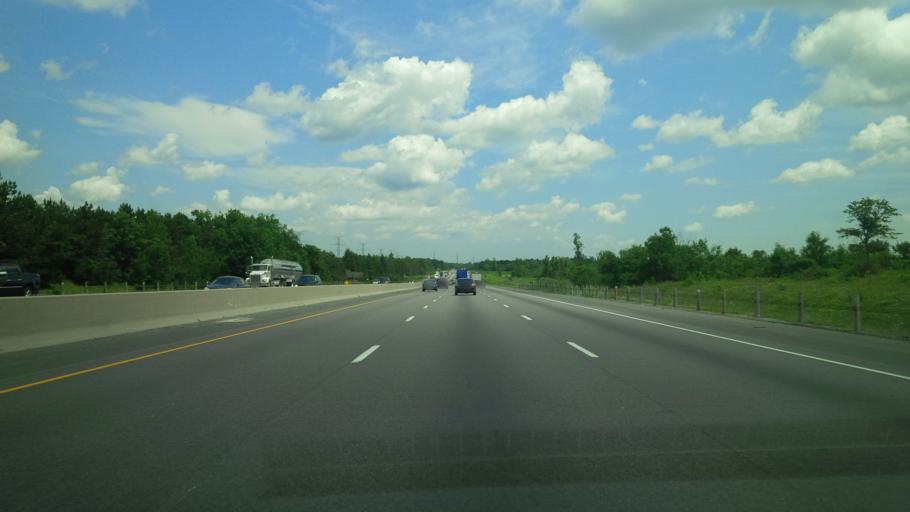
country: CA
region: Ontario
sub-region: Wellington County
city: Guelph
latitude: 43.4630
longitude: -80.0933
